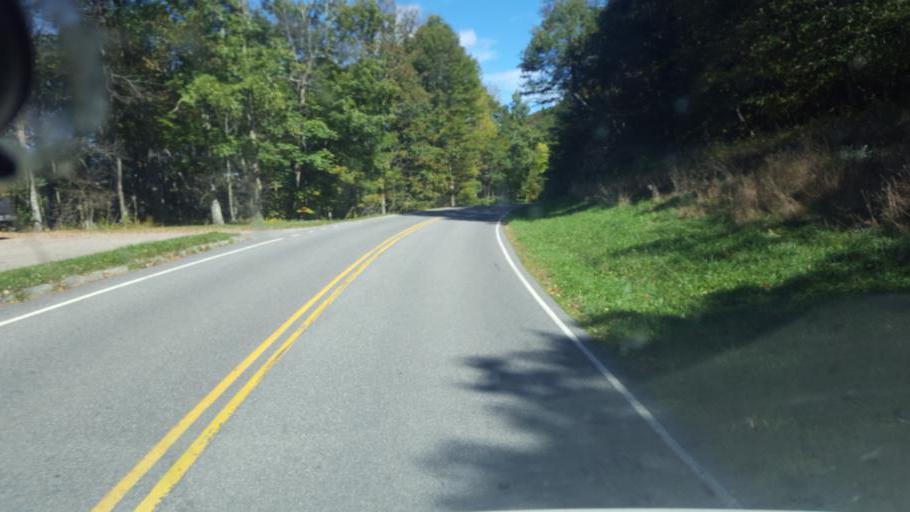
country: US
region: Virginia
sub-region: Page County
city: Stanley
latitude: 38.4524
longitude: -78.4669
